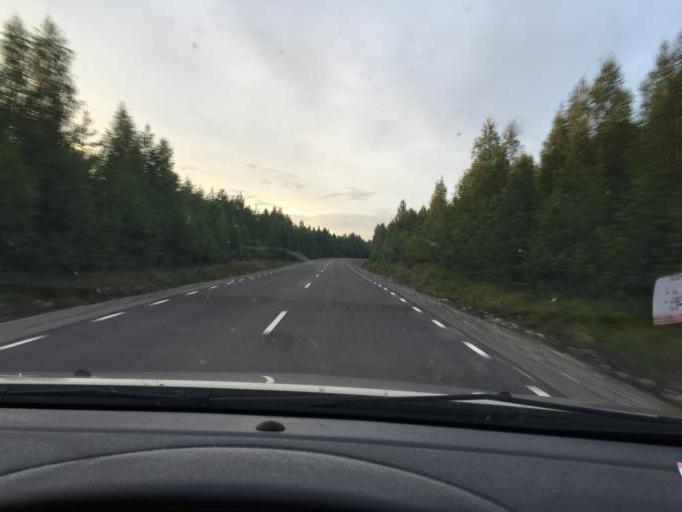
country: SE
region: Norrbotten
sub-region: Lulea Kommun
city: Ranea
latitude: 66.0477
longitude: 22.2049
